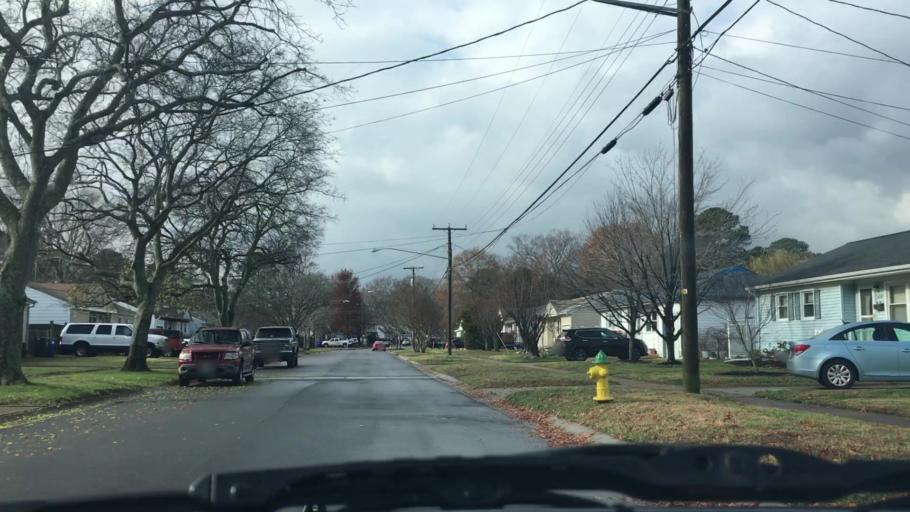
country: US
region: Virginia
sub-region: City of Norfolk
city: Norfolk
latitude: 36.9290
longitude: -76.2332
